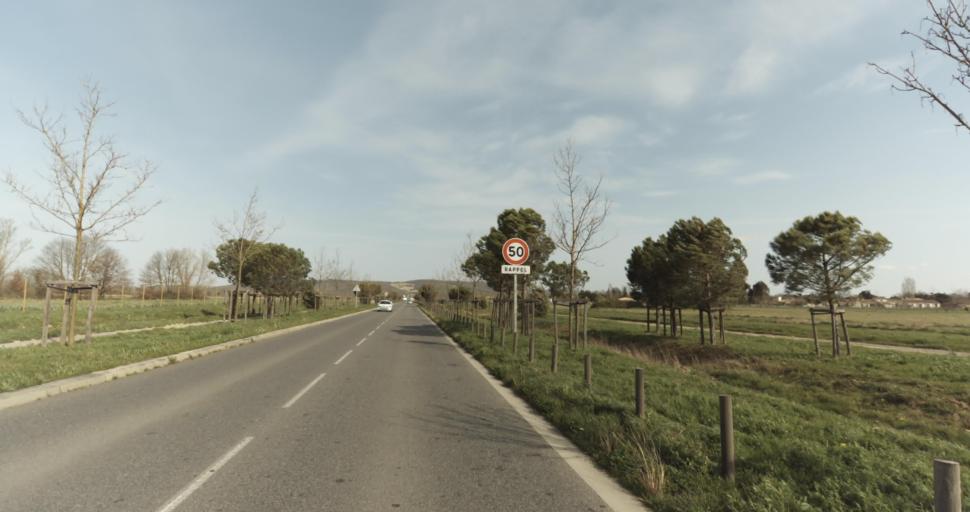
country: FR
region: Midi-Pyrenees
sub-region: Departement du Tarn
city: Saint-Sulpice-la-Pointe
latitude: 43.7587
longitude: 1.6585
